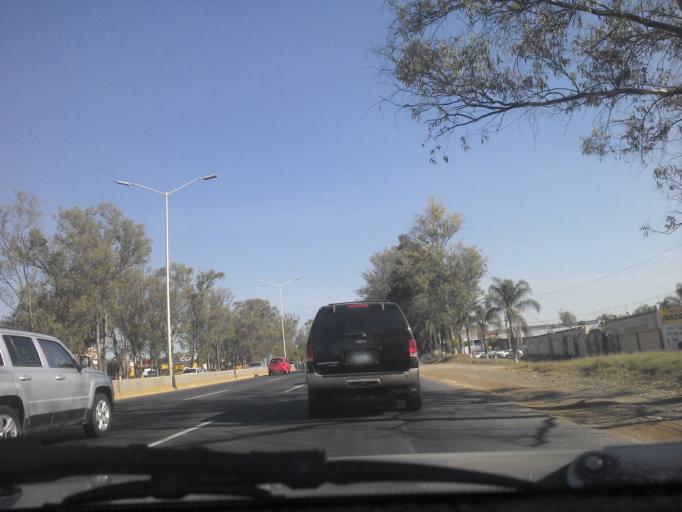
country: MX
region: Jalisco
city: Guadalajara
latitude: 20.6513
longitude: -103.4445
